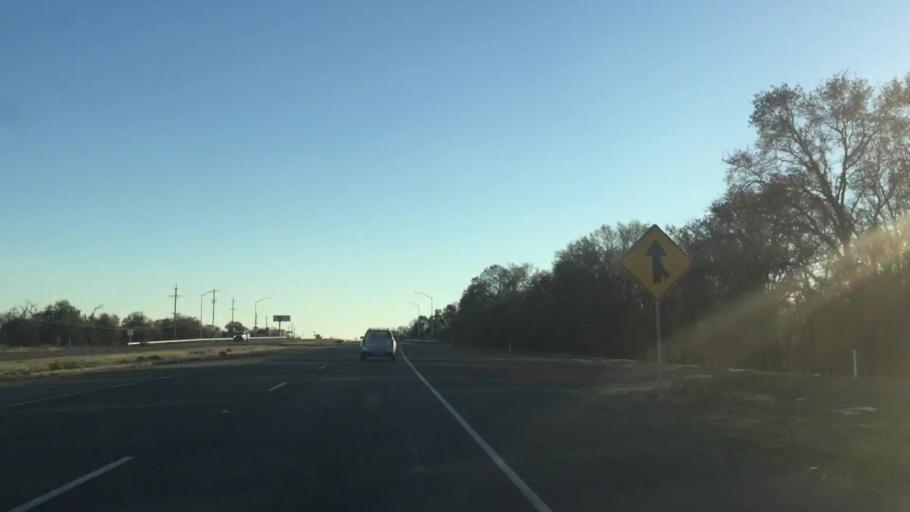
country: US
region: California
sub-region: Yuba County
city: Plumas Lake
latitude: 38.9770
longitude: -121.5432
